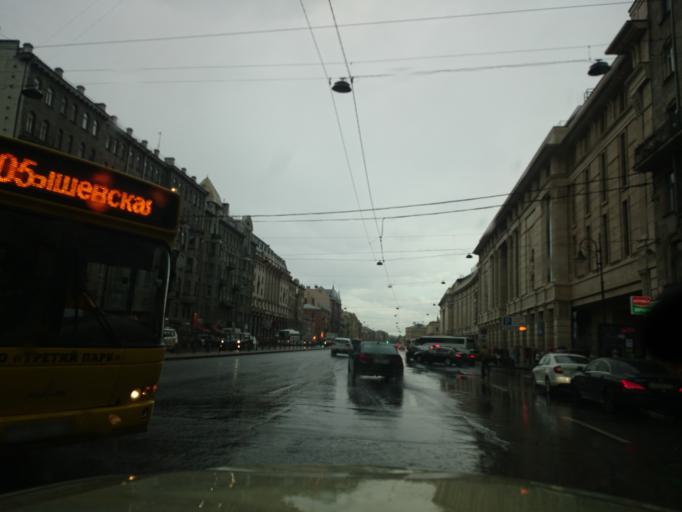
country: RU
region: St.-Petersburg
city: Centralniy
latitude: 59.9265
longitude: 30.3585
